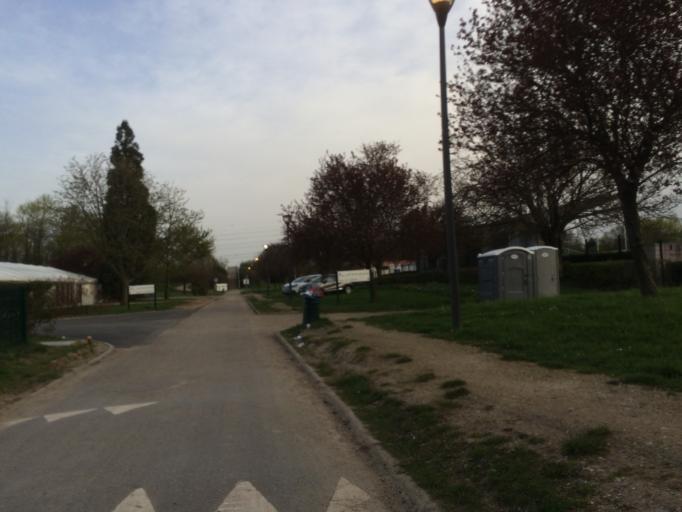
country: FR
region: Ile-de-France
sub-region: Departement de l'Essonne
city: Massy
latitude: 48.7309
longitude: 2.2948
